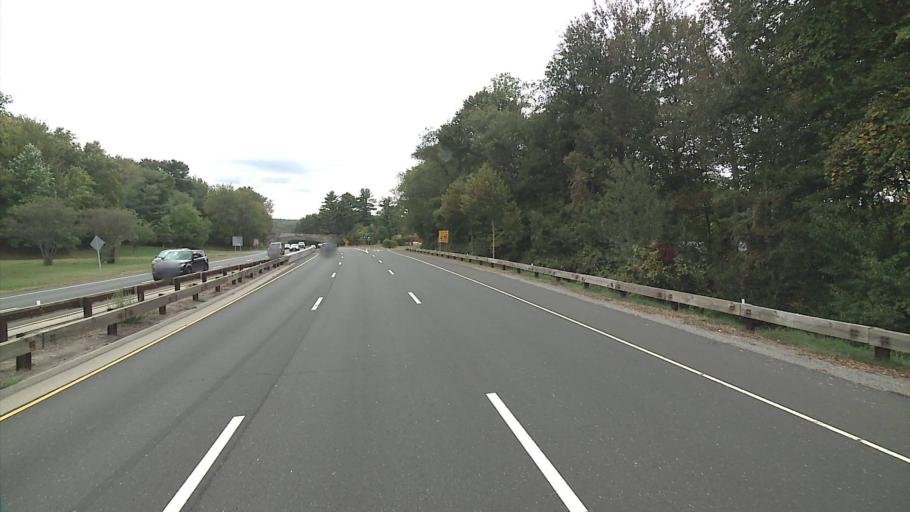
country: US
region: Connecticut
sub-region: Fairfield County
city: Trumbull
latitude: 41.2290
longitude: -73.2431
